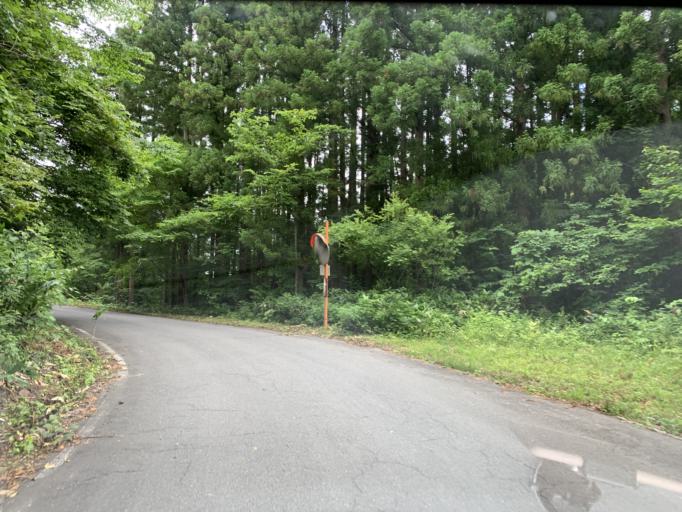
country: JP
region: Iwate
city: Ichinoseki
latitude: 38.9689
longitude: 140.9131
